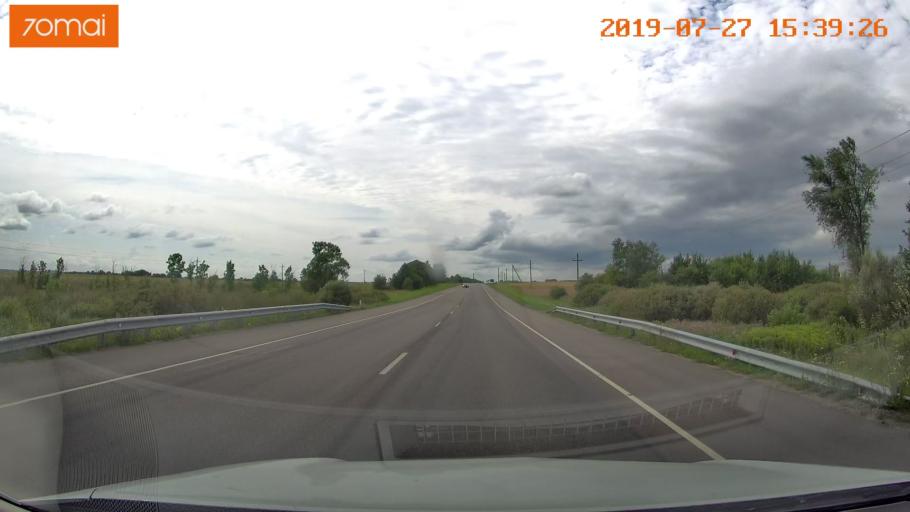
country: RU
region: Kaliningrad
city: Gusev
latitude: 54.6055
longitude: 22.2872
